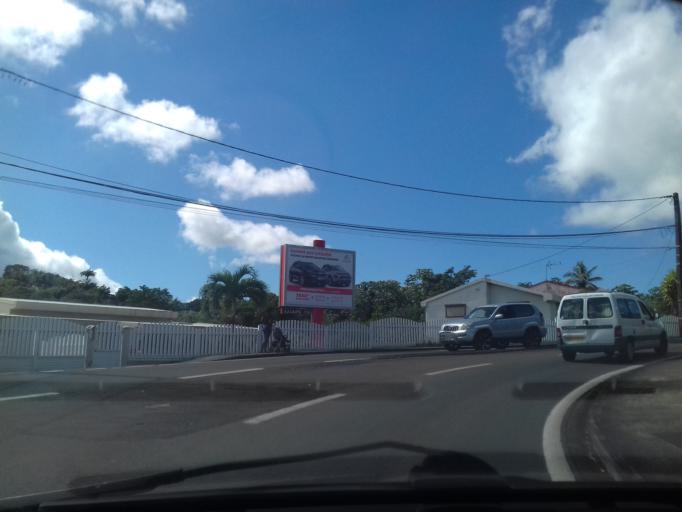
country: MQ
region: Martinique
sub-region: Martinique
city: Saint-Joseph
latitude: 14.6727
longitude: -61.0317
